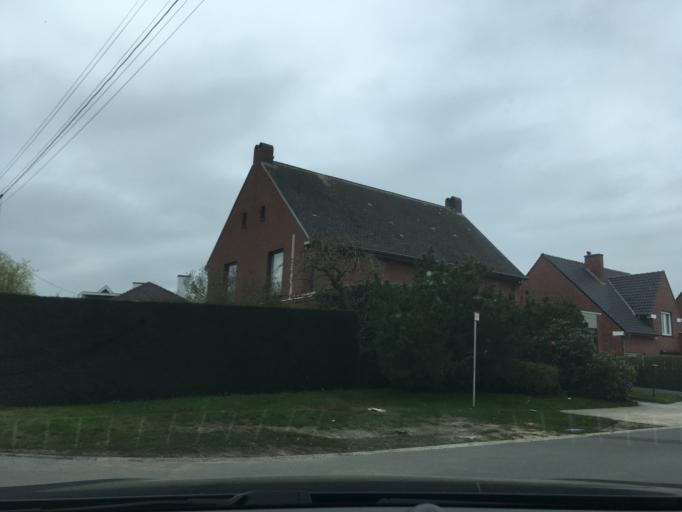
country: BE
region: Flanders
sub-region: Provincie West-Vlaanderen
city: Kortemark
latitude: 51.0260
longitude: 3.0400
